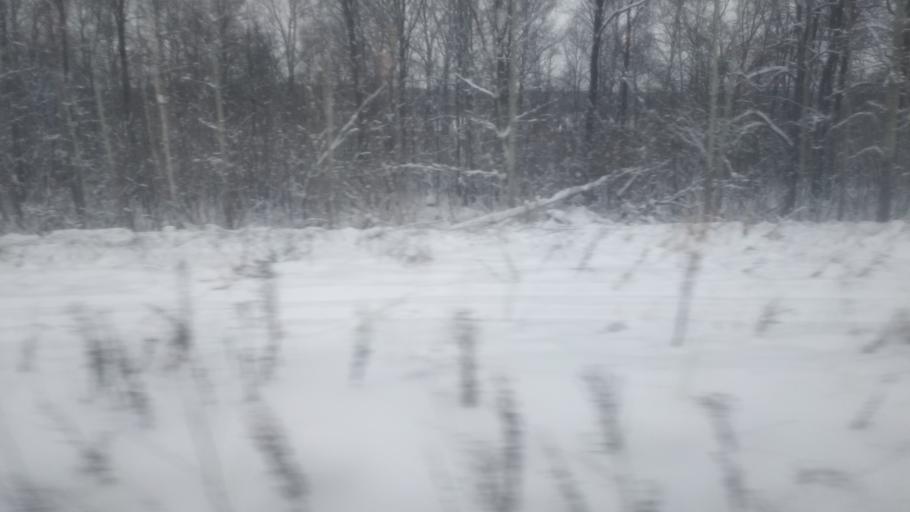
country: RU
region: Udmurtiya
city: Sigayevo
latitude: 56.4525
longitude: 53.7043
